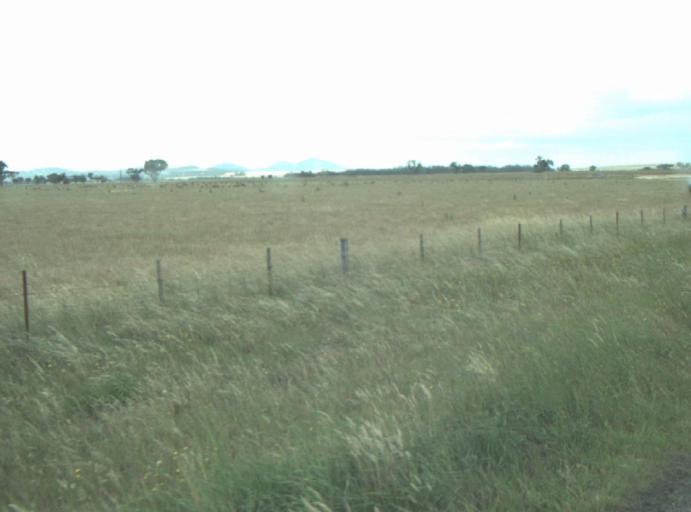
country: AU
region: Victoria
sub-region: Greater Geelong
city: Lara
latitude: -37.8529
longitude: 144.3532
